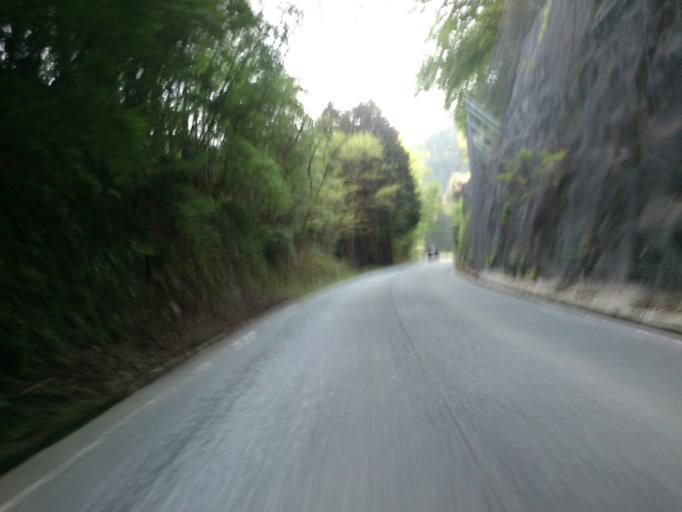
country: JP
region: Kyoto
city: Fukuchiyama
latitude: 35.2567
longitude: 135.0672
